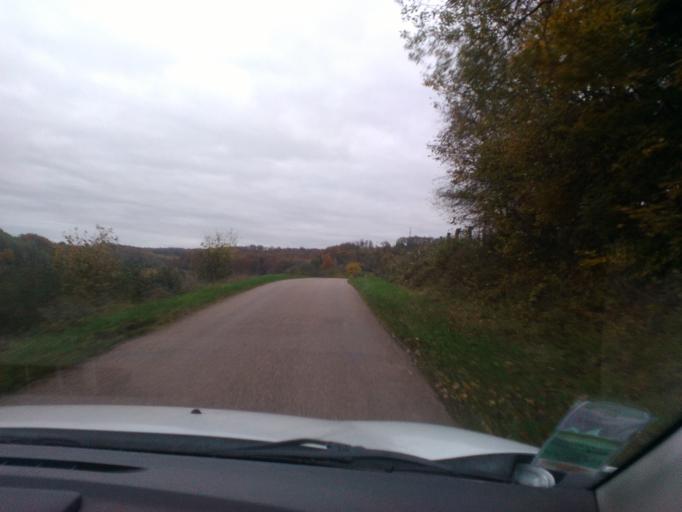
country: FR
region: Lorraine
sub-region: Departement des Vosges
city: Mirecourt
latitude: 48.3095
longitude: 6.2108
